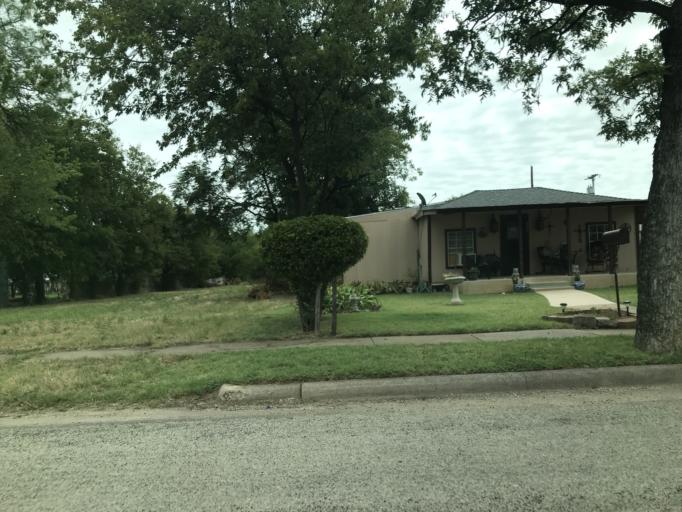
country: US
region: Texas
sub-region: Taylor County
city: Abilene
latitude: 32.4381
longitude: -99.7363
